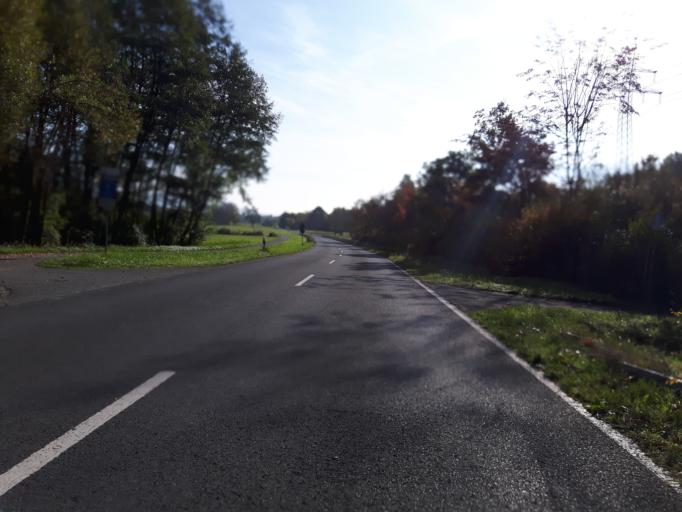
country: DE
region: Bavaria
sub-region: Regierungsbezirk Unterfranken
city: Worth am Main
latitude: 49.8058
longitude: 9.1373
